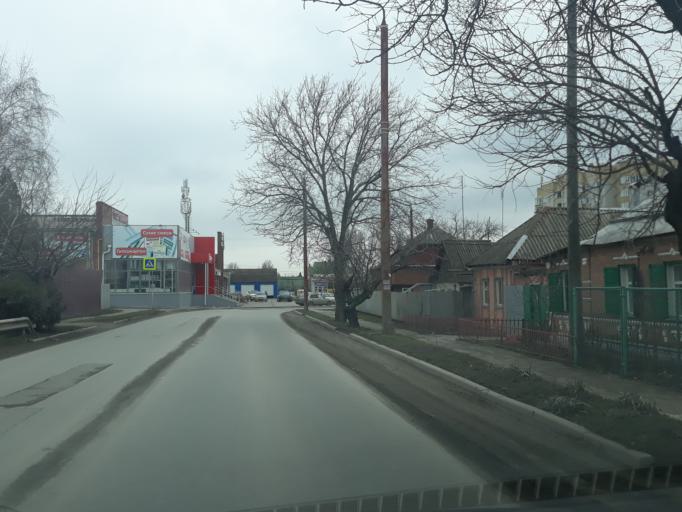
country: RU
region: Rostov
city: Taganrog
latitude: 47.2630
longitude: 38.8944
